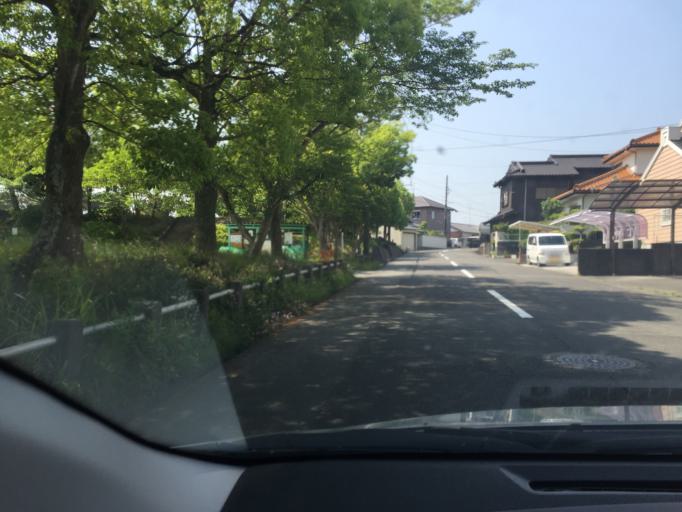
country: JP
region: Shizuoka
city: Kakegawa
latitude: 34.7895
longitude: 138.0295
